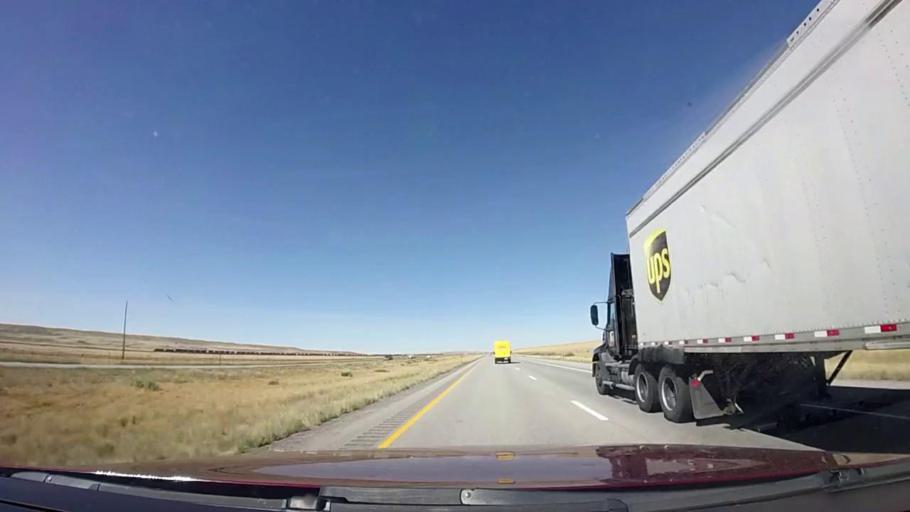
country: US
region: Wyoming
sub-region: Carbon County
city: Rawlins
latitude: 41.6595
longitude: -108.0767
